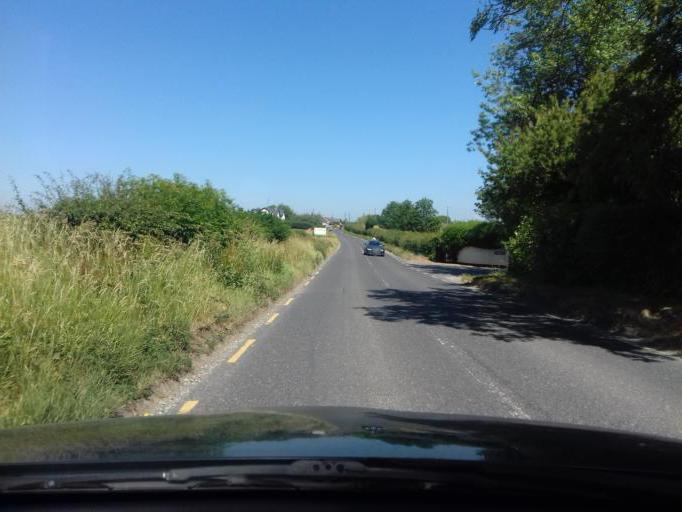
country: IE
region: Leinster
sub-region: Fingal County
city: Swords
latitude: 53.4954
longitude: -6.2699
